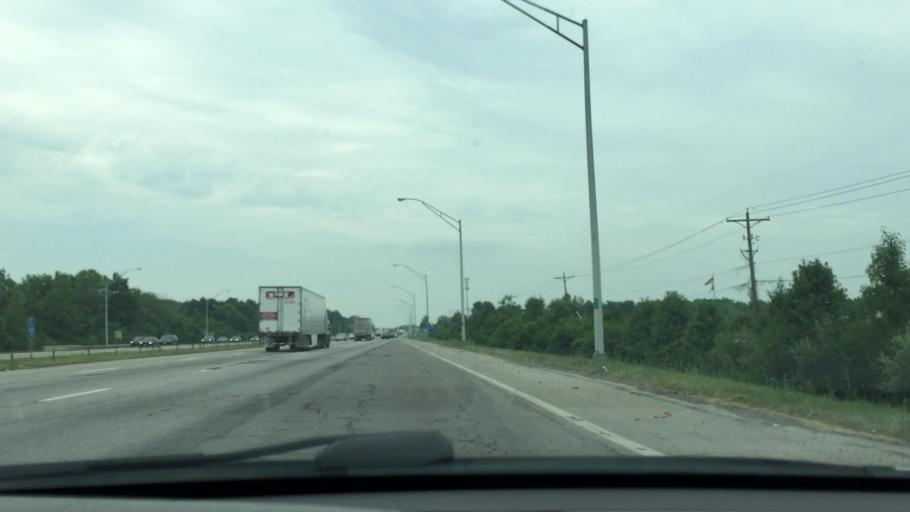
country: US
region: Ohio
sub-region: Franklin County
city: Reynoldsburg
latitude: 39.9321
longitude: -82.8237
